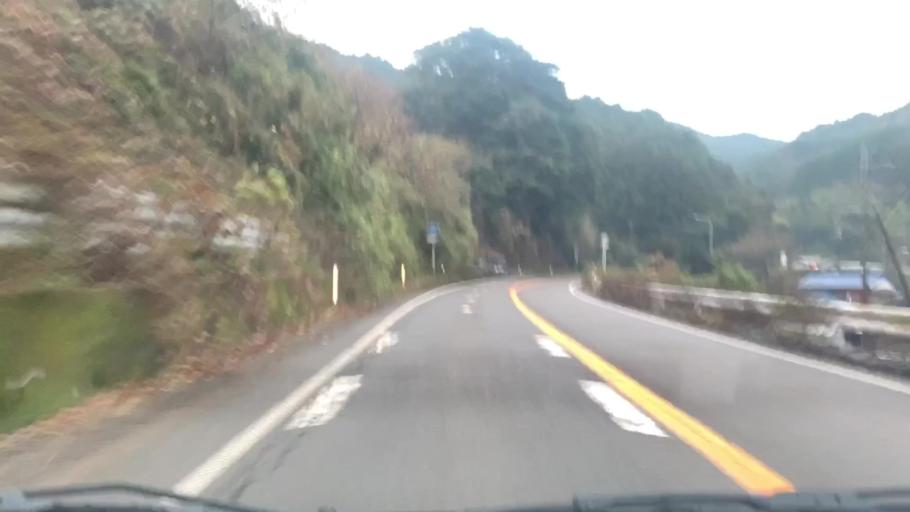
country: JP
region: Saga Prefecture
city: Ureshinomachi-shimojuku
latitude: 33.0698
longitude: 129.9626
